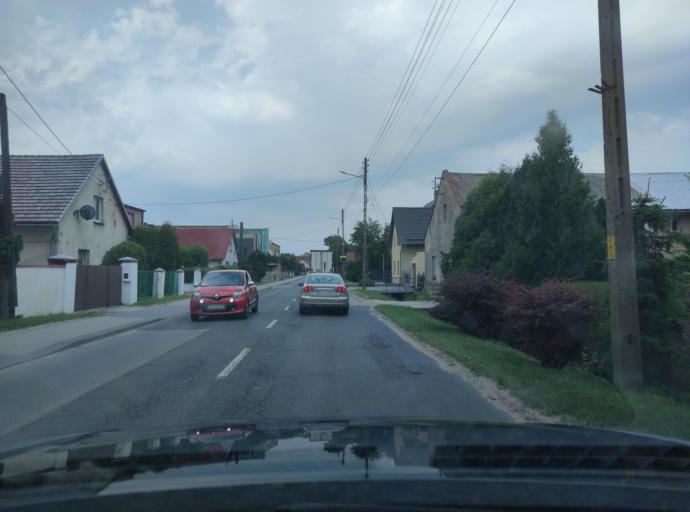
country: PL
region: Opole Voivodeship
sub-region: Powiat strzelecki
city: Strzelce Opolskie
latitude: 50.5014
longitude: 18.2920
